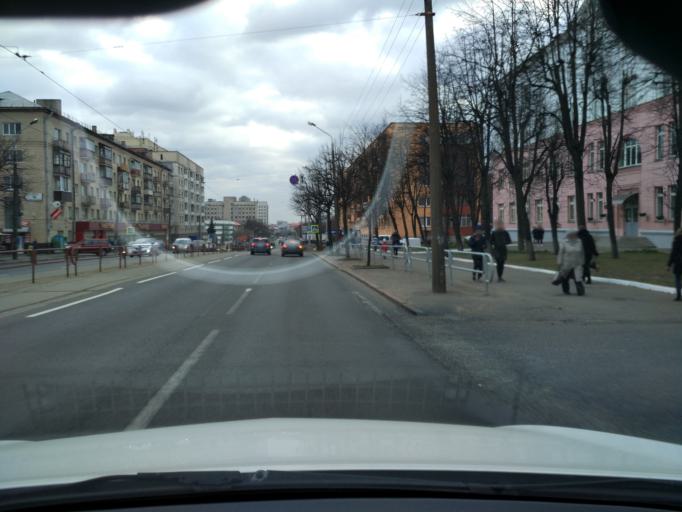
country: BY
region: Minsk
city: Minsk
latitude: 53.9278
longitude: 27.5957
